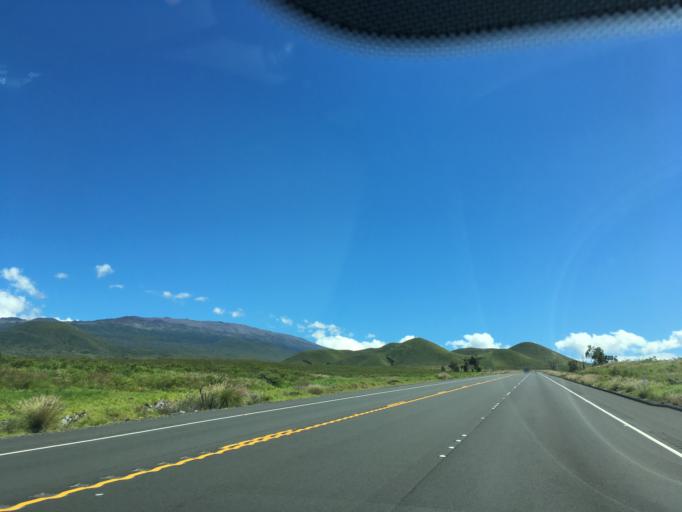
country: US
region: Hawaii
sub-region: Hawaii County
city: Waikoloa
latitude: 19.7897
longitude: -155.6586
